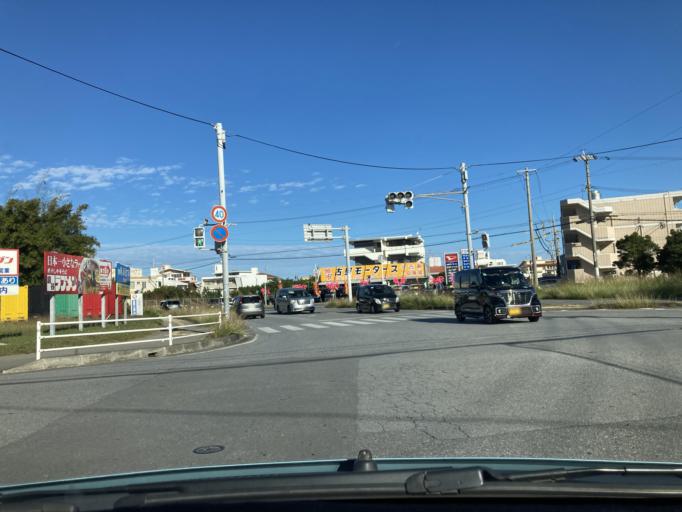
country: JP
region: Okinawa
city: Okinawa
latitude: 26.3699
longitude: 127.7467
